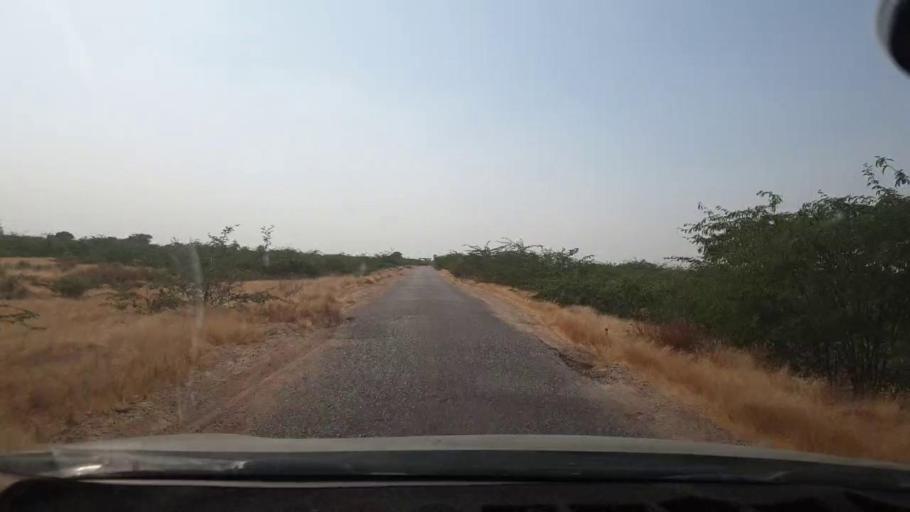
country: PK
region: Sindh
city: Malir Cantonment
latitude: 25.1036
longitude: 67.1974
